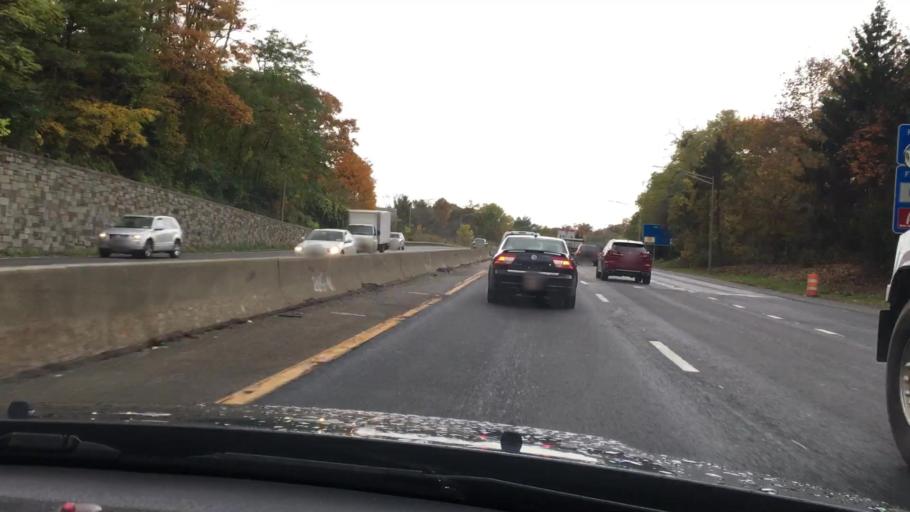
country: US
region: New York
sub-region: Orange County
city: Balmville
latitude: 41.5207
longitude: -74.0135
